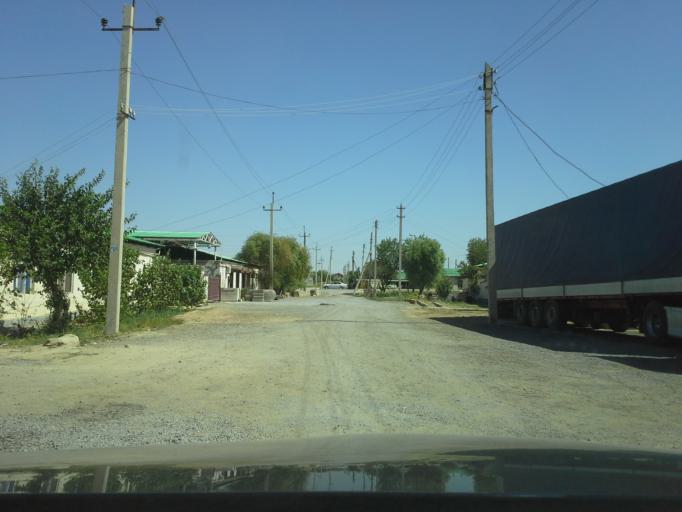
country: TM
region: Ahal
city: Ashgabat
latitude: 38.0101
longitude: 58.3066
